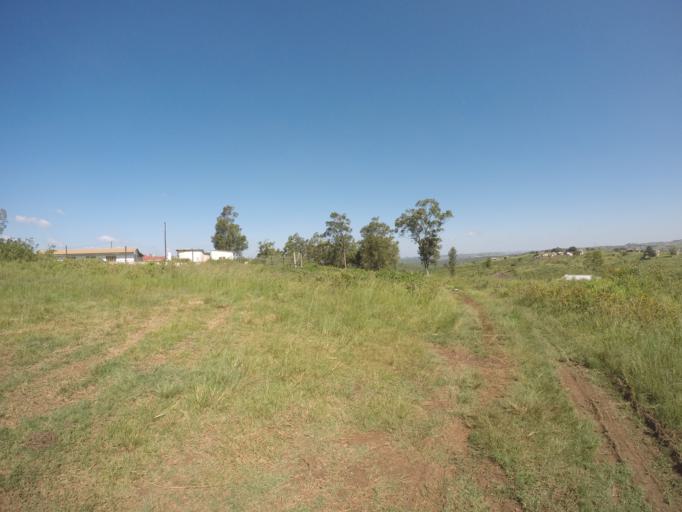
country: ZA
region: KwaZulu-Natal
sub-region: uThungulu District Municipality
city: Empangeni
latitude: -28.5643
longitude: 31.7008
